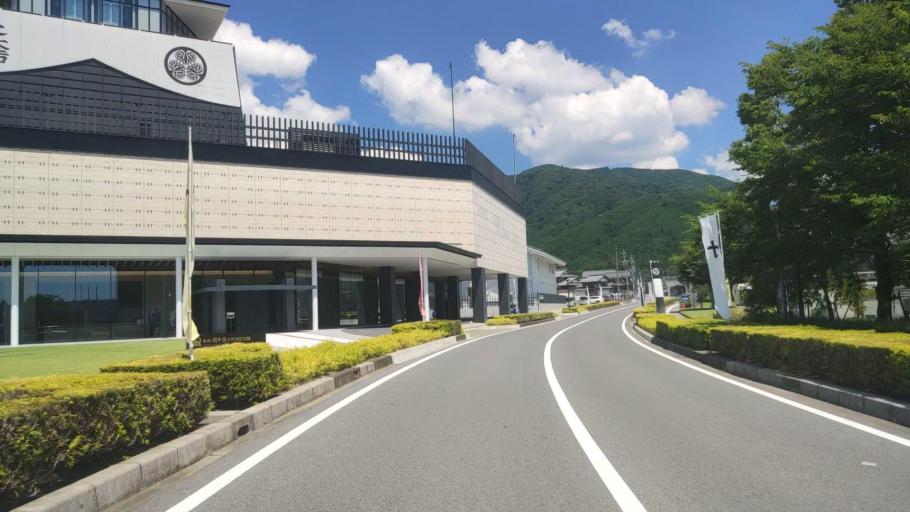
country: JP
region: Gifu
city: Tarui
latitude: 35.3654
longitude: 136.4667
